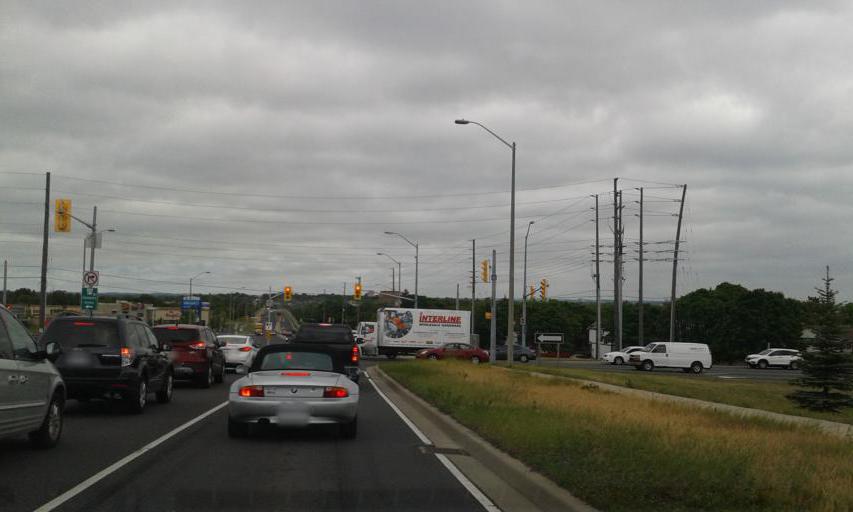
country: CA
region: Ontario
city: Oshawa
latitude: 43.8774
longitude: -78.8765
